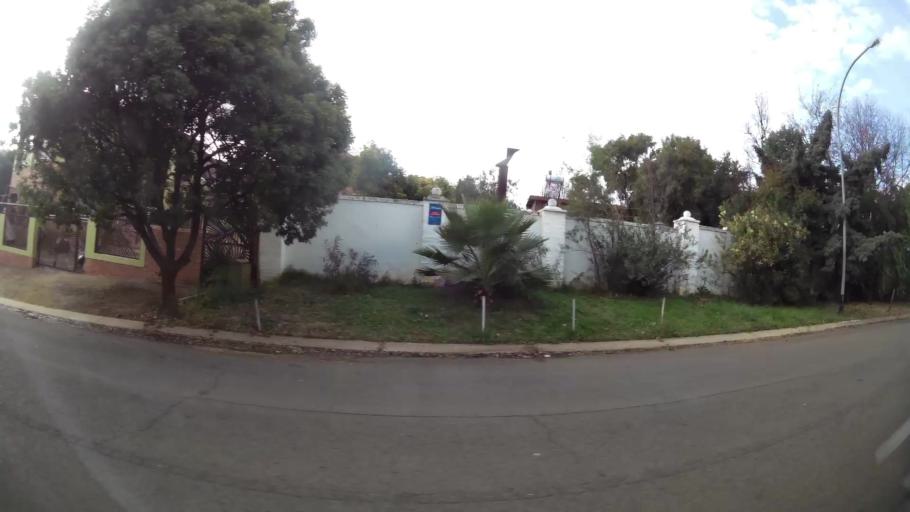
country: ZA
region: Orange Free State
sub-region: Mangaung Metropolitan Municipality
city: Bloemfontein
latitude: -29.0843
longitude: 26.1960
